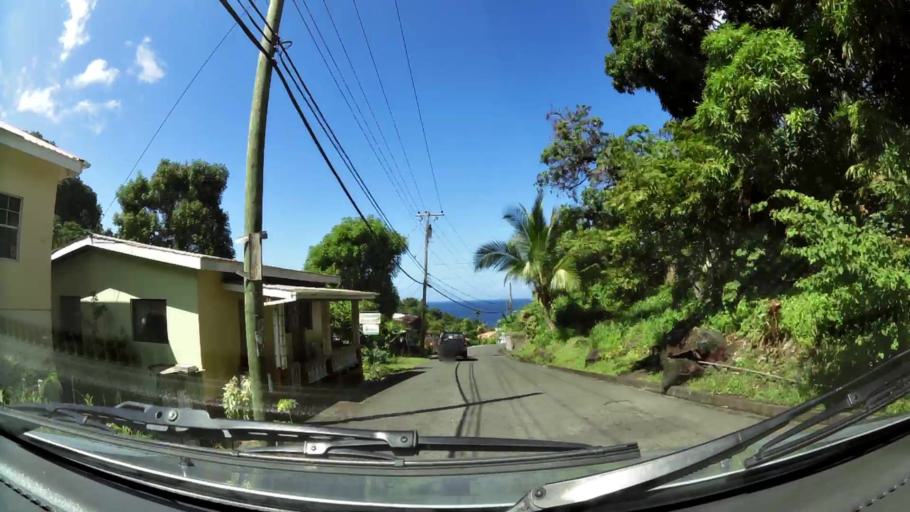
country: GD
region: Saint John
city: Gouyave
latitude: 12.1256
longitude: -61.7461
